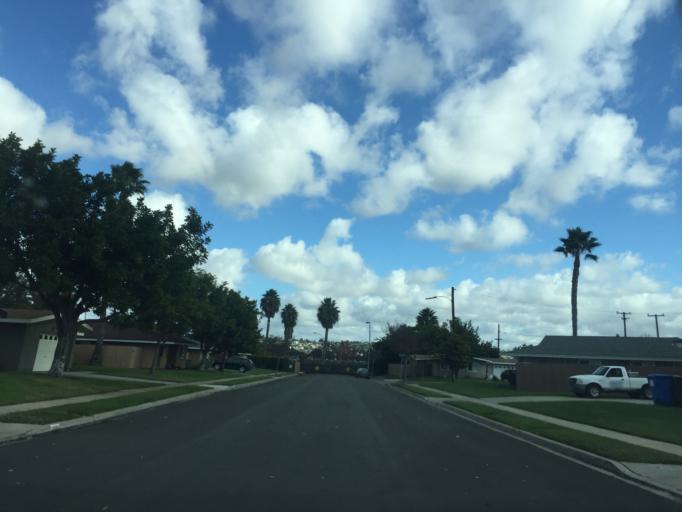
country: US
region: California
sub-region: San Diego County
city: La Jolla
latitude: 32.7997
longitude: -117.2272
